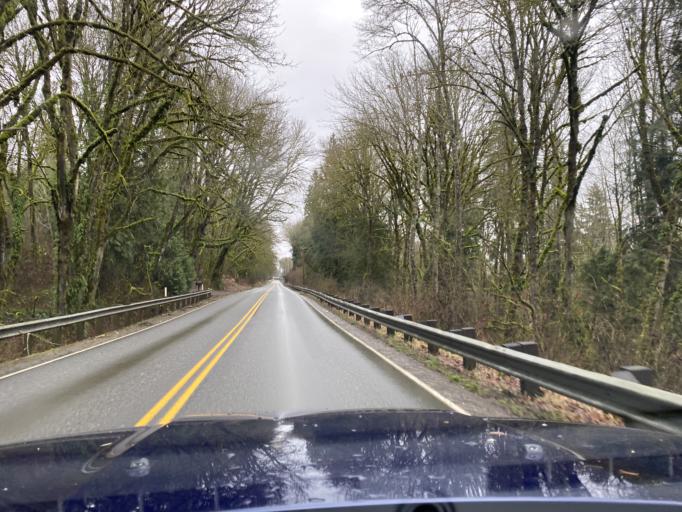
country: US
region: Washington
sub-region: King County
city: Duvall
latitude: 47.7590
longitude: -122.0035
